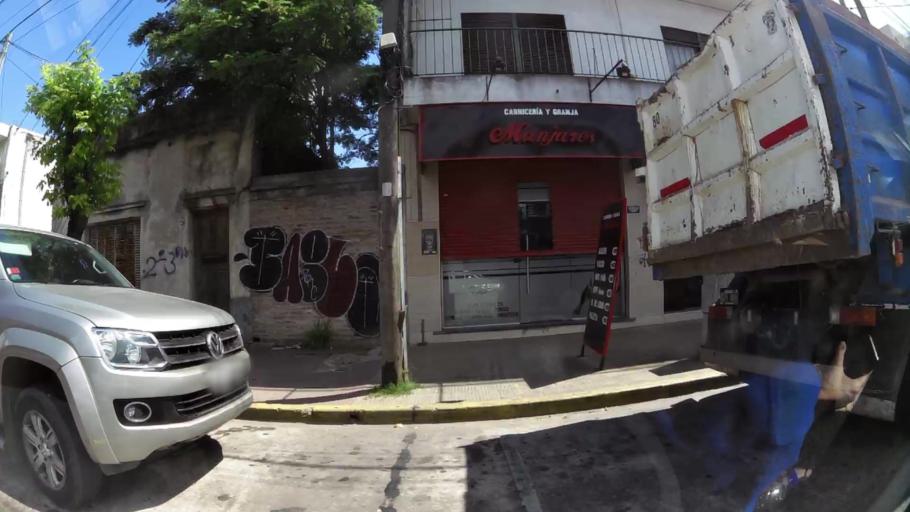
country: AR
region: Buenos Aires
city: San Justo
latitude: -34.6808
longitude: -58.5593
